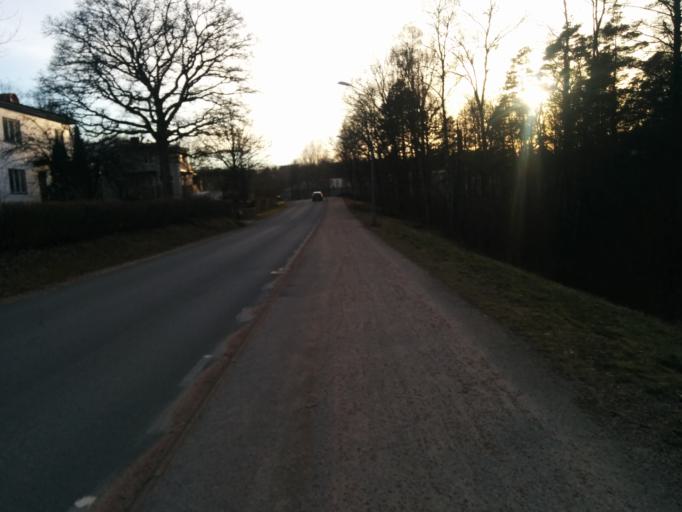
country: SE
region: Joenkoeping
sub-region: Gislaveds Kommun
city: Smalandsstenar
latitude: 57.1990
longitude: 13.2803
